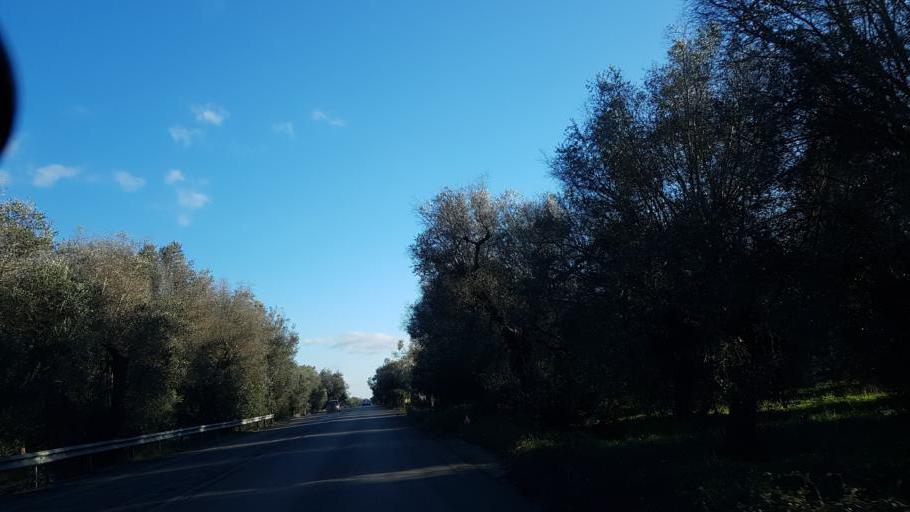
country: IT
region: Apulia
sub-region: Provincia di Brindisi
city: San Pietro Vernotico
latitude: 40.4652
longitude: 18.0171
